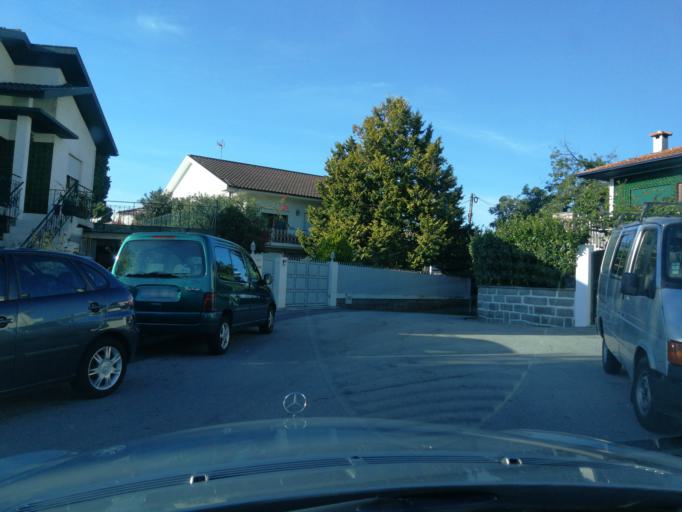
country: PT
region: Braga
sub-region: Vila Nova de Famalicao
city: Vila Nova de Famalicao
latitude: 41.4260
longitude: -8.5192
